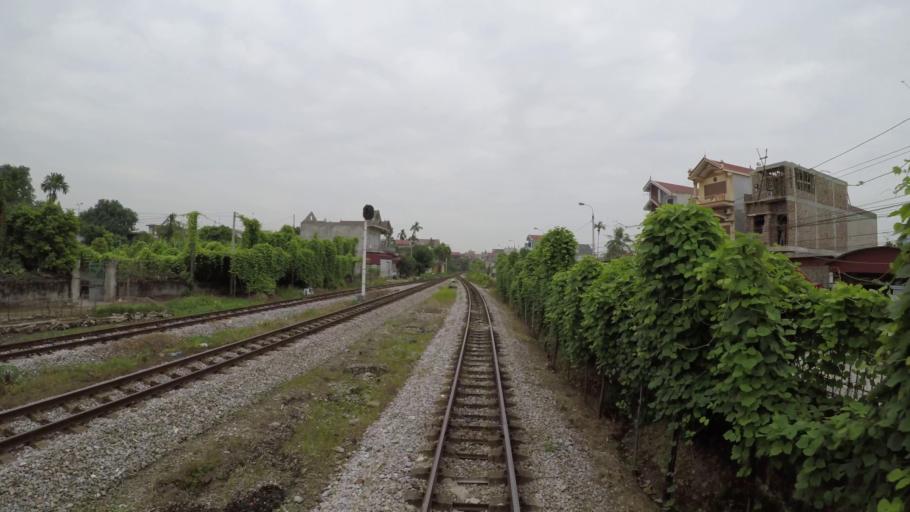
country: VN
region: Hai Duong
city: Phu Thai
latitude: 20.9691
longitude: 106.4995
